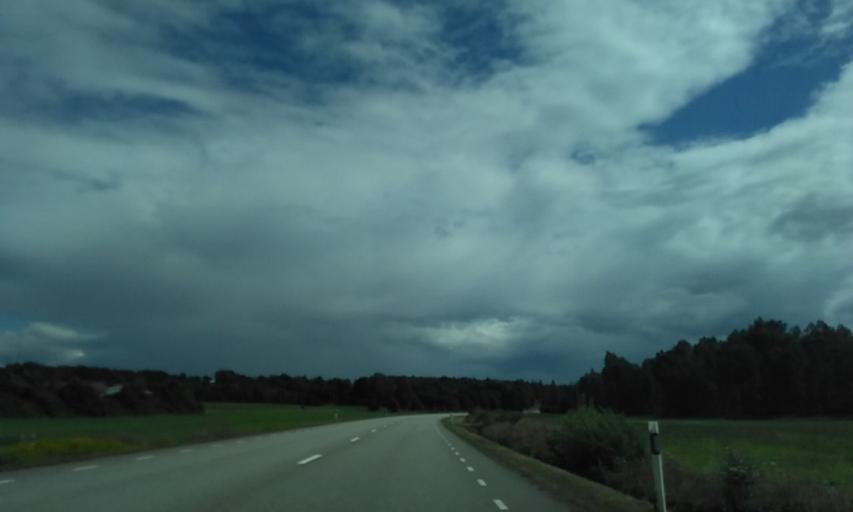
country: SE
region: Vaestra Goetaland
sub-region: Vargarda Kommun
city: Vargarda
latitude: 58.0212
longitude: 12.8095
